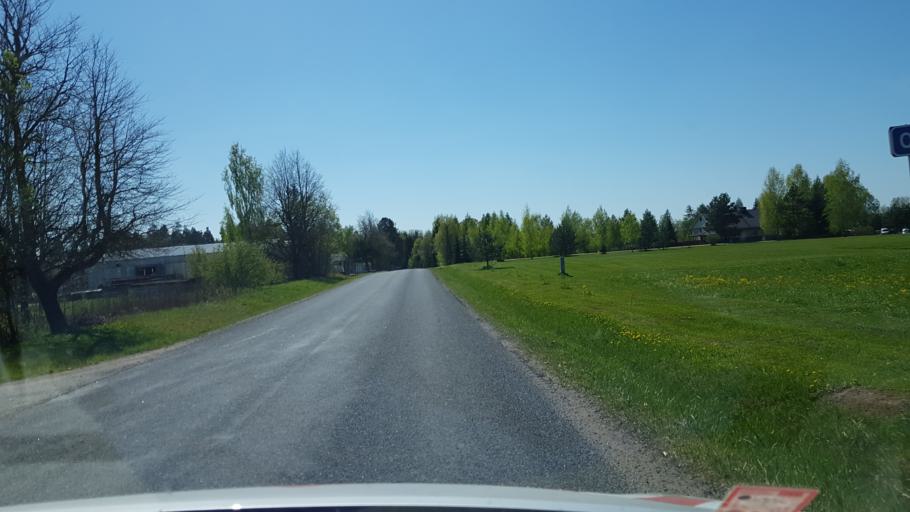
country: EE
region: Vorumaa
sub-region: Antsla vald
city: Vana-Antsla
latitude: 57.8187
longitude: 26.5202
